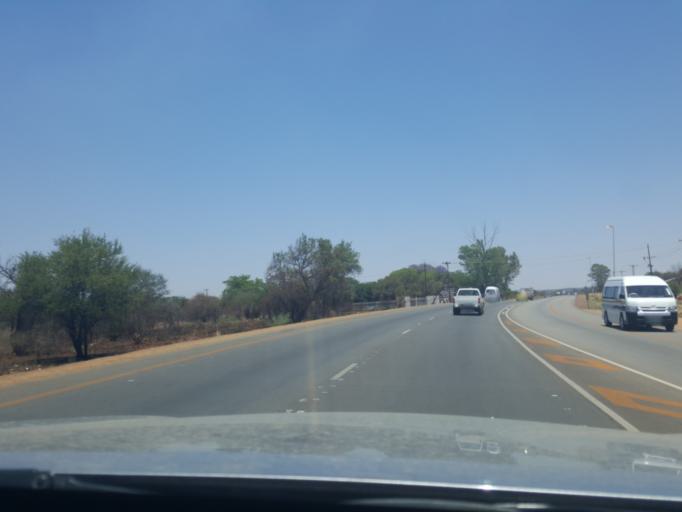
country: ZA
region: North-West
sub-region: Ngaka Modiri Molema District Municipality
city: Zeerust
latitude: -25.5531
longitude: 26.0710
